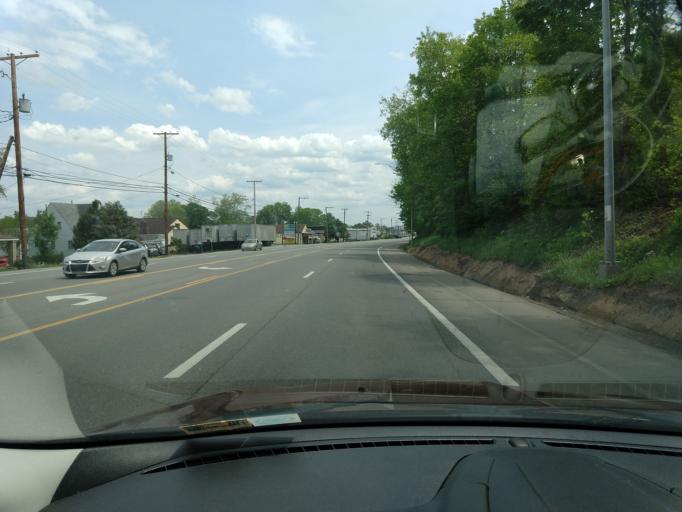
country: US
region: West Virginia
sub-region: Kanawha County
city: Dunbar
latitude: 38.3726
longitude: -81.7728
